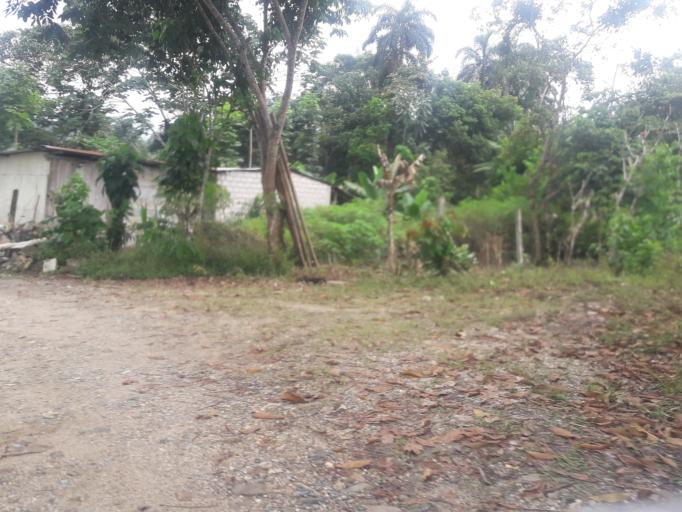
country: EC
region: Napo
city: Tena
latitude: -0.9795
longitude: -77.8472
